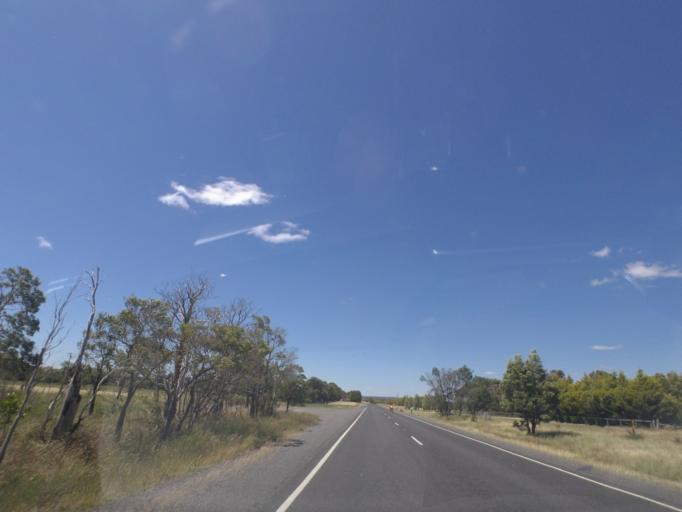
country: AU
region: Victoria
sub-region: Mount Alexander
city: Castlemaine
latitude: -37.2162
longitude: 144.3478
